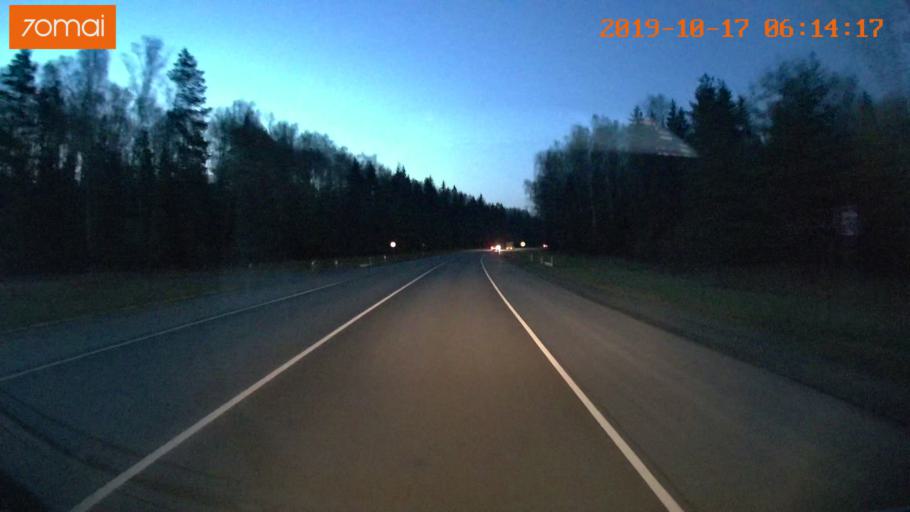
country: RU
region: Ivanovo
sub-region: Gorod Ivanovo
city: Ivanovo
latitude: 56.8875
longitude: 40.9425
